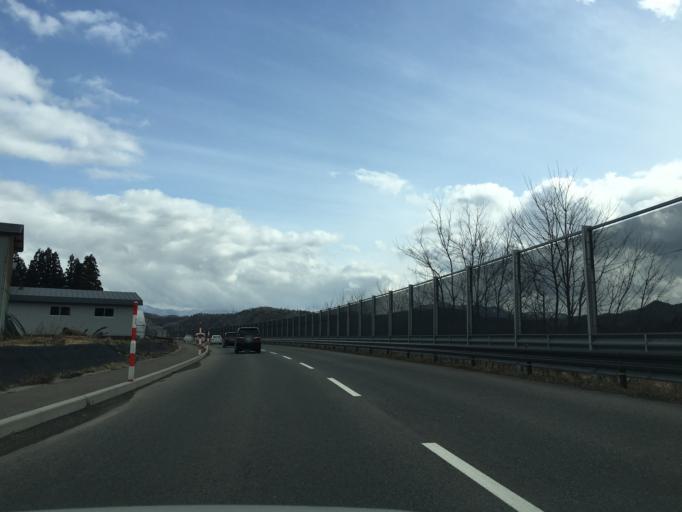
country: JP
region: Akita
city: Hanawa
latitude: 40.2321
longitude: 140.7022
